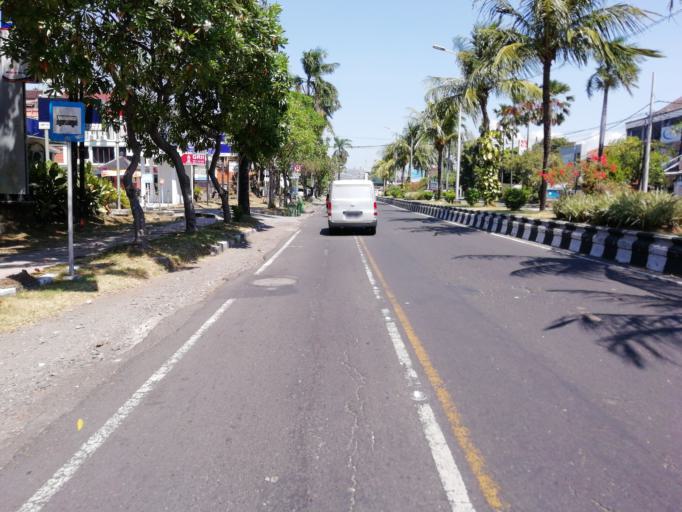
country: ID
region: Bali
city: Denpasar
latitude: -8.6756
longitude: 115.2178
